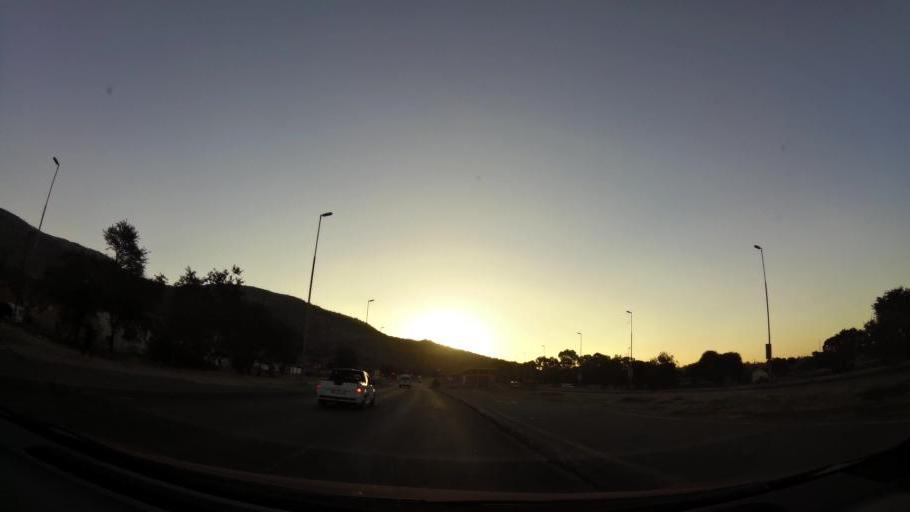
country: ZA
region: North-West
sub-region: Bojanala Platinum District Municipality
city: Rustenburg
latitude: -25.6411
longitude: 27.2015
